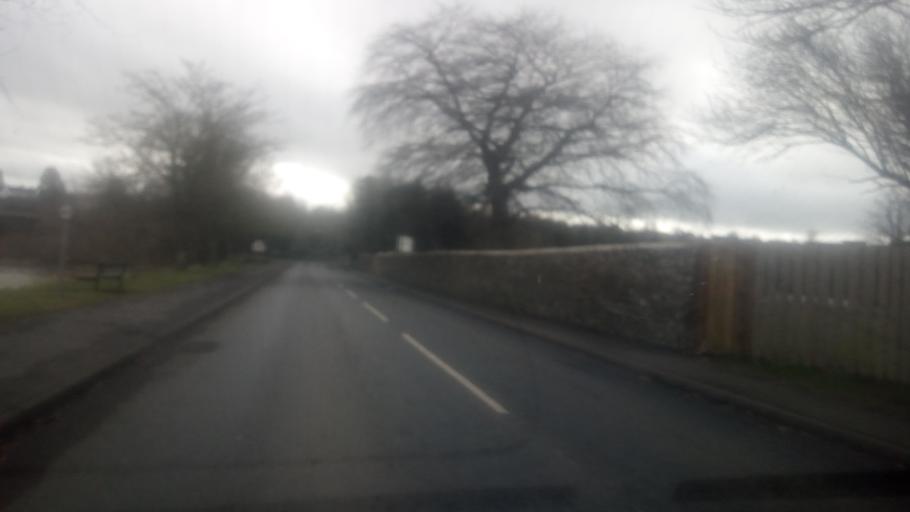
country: GB
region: Scotland
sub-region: The Scottish Borders
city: Kelso
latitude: 55.5964
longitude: -2.4367
